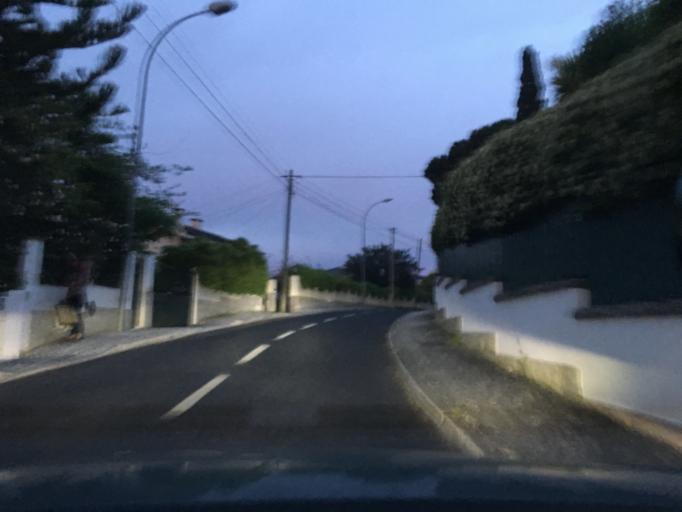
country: PT
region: Lisbon
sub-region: Oeiras
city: Terrugem
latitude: 38.7032
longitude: -9.2803
